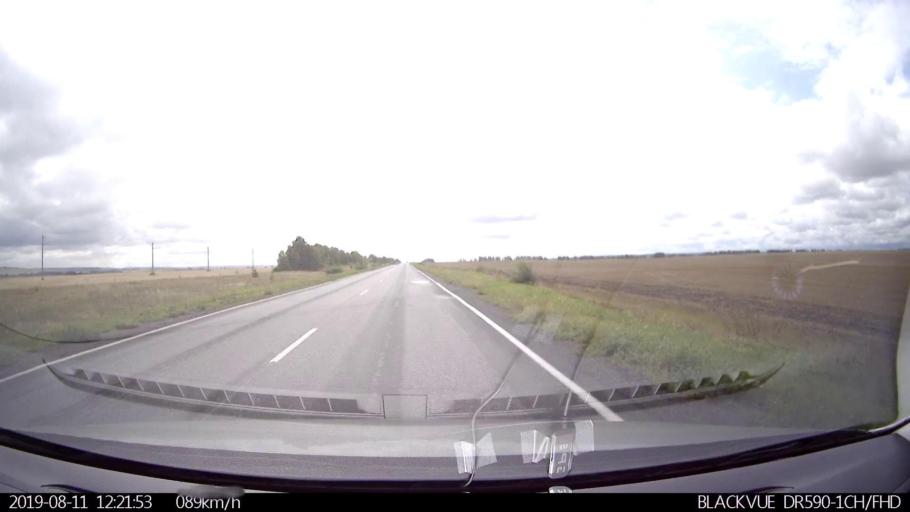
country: RU
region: Ulyanovsk
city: Ignatovka
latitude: 53.9154
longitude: 47.9562
